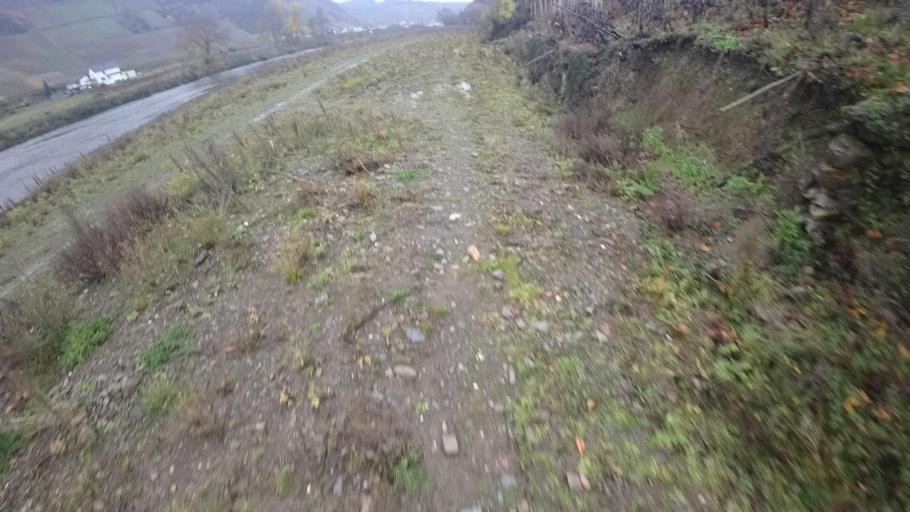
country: DE
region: Rheinland-Pfalz
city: Rech
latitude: 50.5171
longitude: 7.0417
